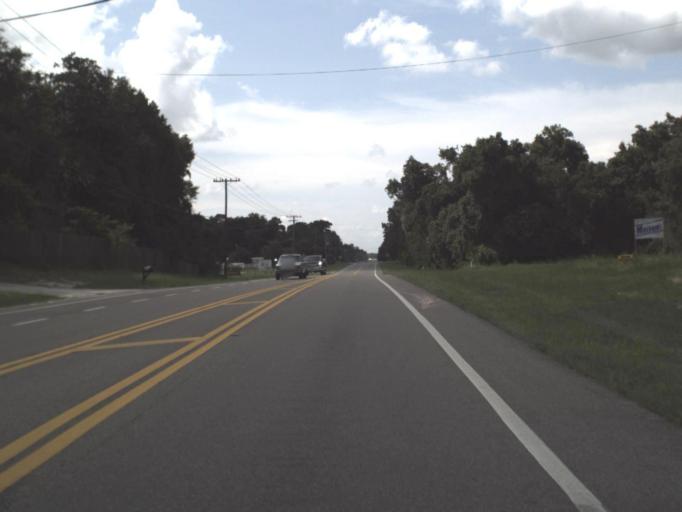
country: US
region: Florida
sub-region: Citrus County
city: Floral City
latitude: 28.7852
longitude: -82.2992
